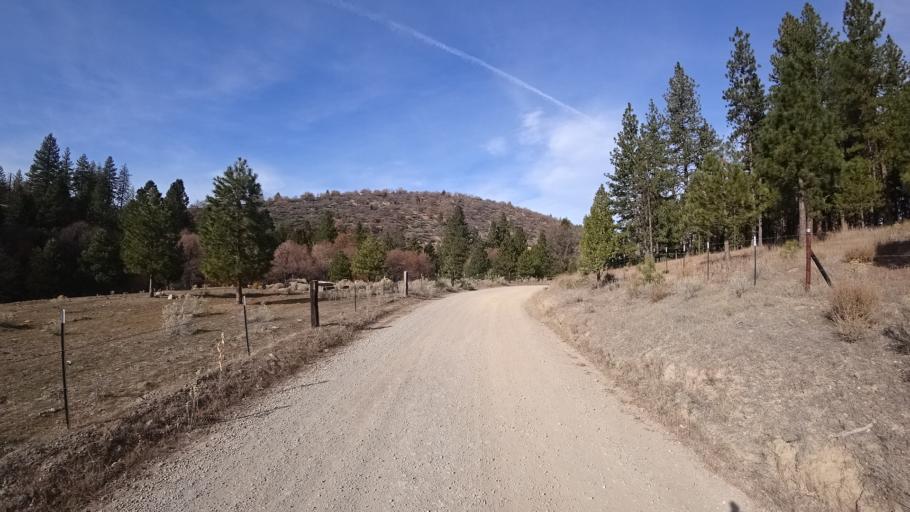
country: US
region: California
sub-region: Siskiyou County
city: Weed
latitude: 41.4342
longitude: -122.4232
